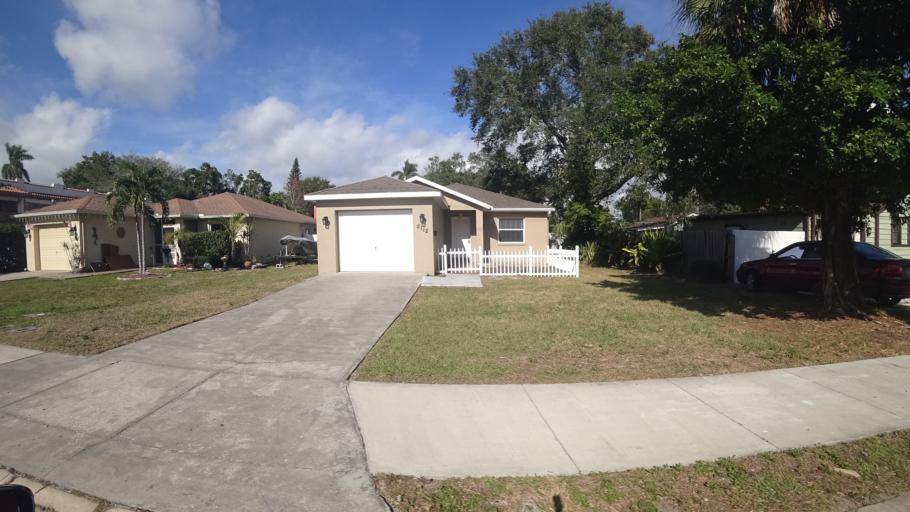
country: US
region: Florida
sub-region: Manatee County
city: Bradenton
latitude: 27.4919
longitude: -82.5826
